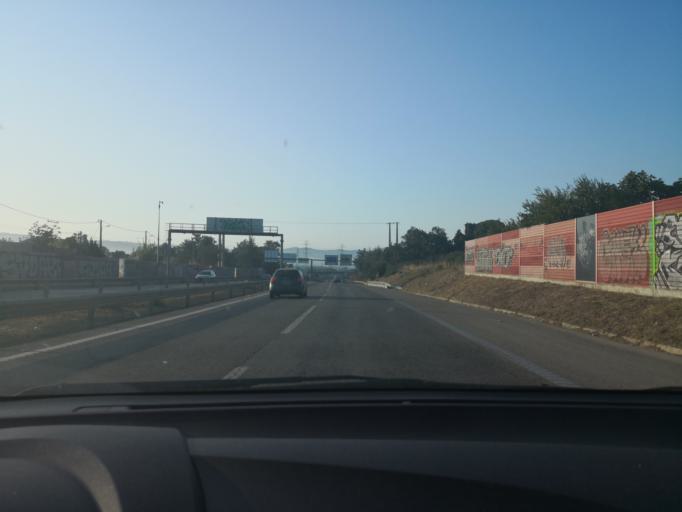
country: PT
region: Setubal
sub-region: Barreiro
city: Santo Antonio da Charneca
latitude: 38.5929
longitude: -9.0208
